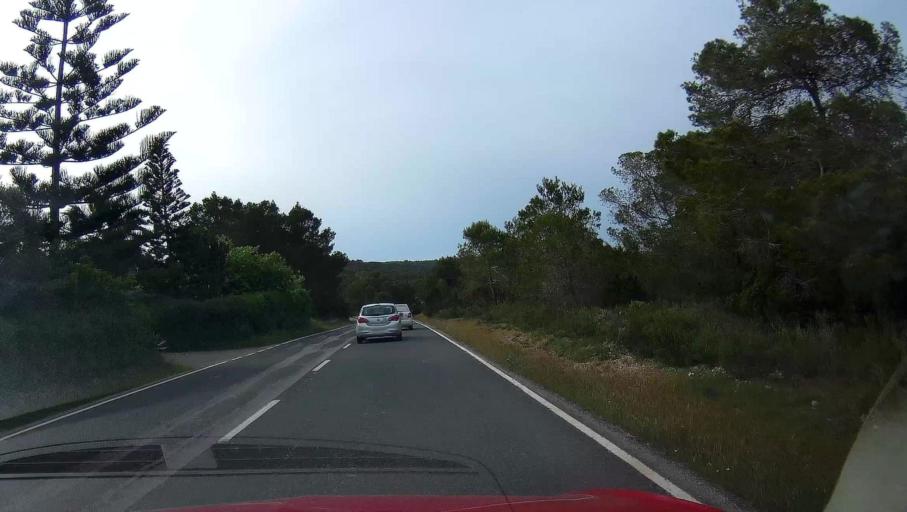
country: ES
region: Balearic Islands
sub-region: Illes Balears
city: Sant Joan de Labritja
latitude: 39.0930
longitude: 1.5002
